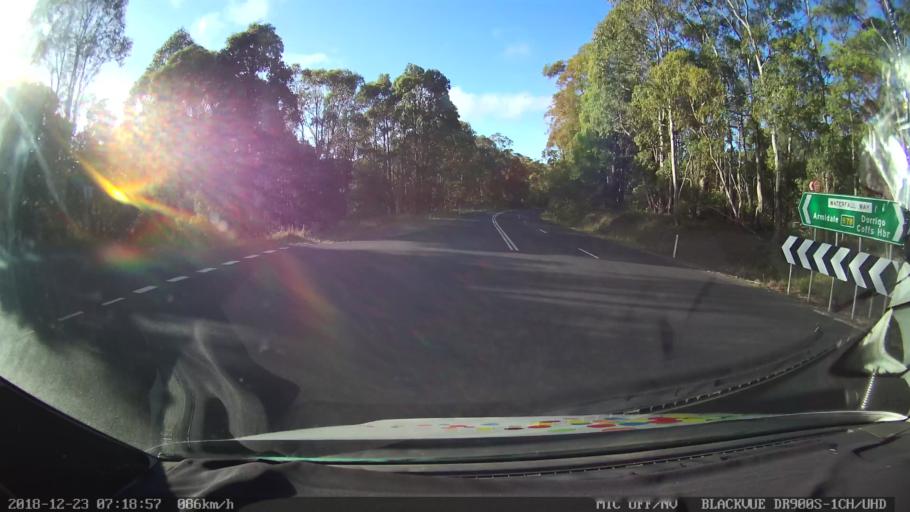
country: AU
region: New South Wales
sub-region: Bellingen
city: Dorrigo
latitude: -30.4809
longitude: 152.2913
